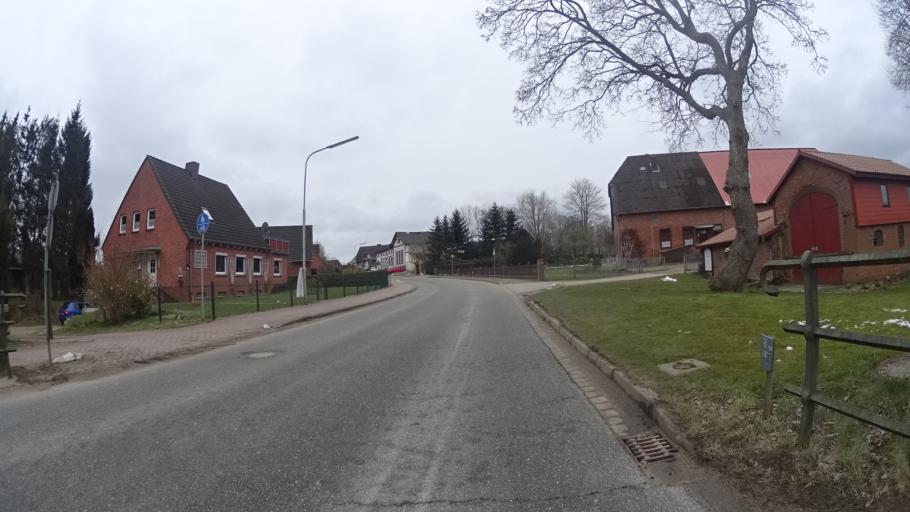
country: DE
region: Schleswig-Holstein
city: Neukirchen
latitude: 54.2044
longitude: 10.5578
